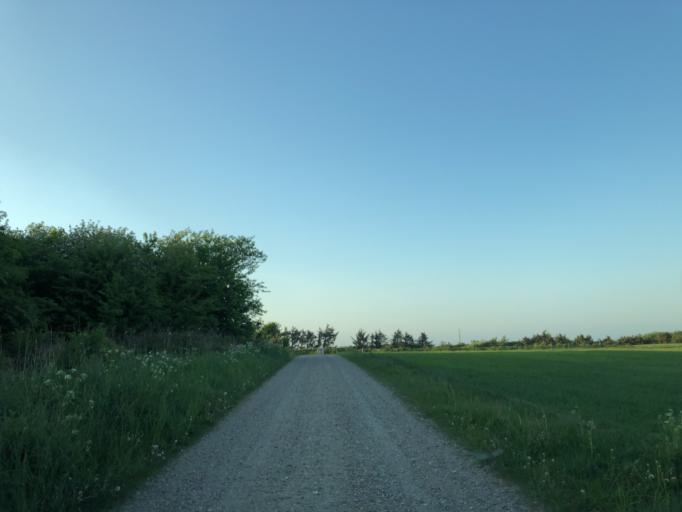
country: DK
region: Central Jutland
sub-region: Holstebro Kommune
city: Ulfborg
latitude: 56.2542
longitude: 8.1604
